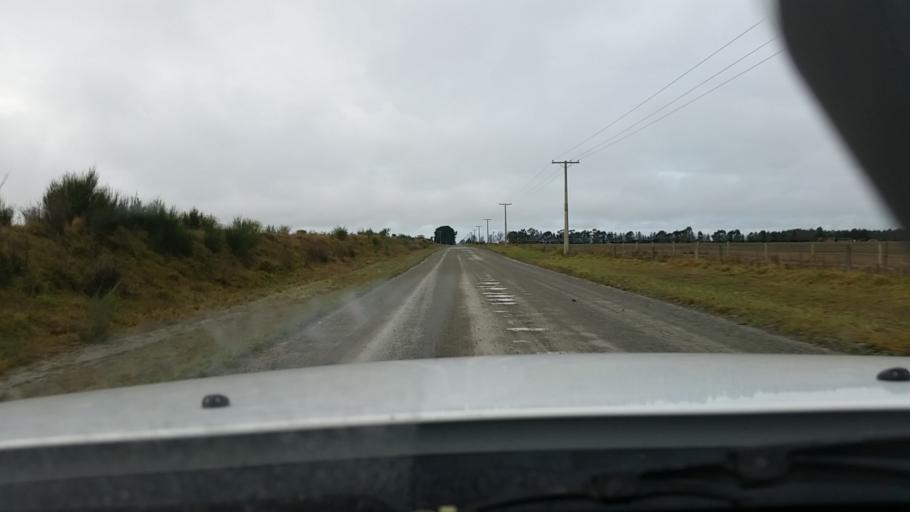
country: NZ
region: Canterbury
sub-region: Timaru District
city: Pleasant Point
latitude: -44.1064
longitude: 171.3801
